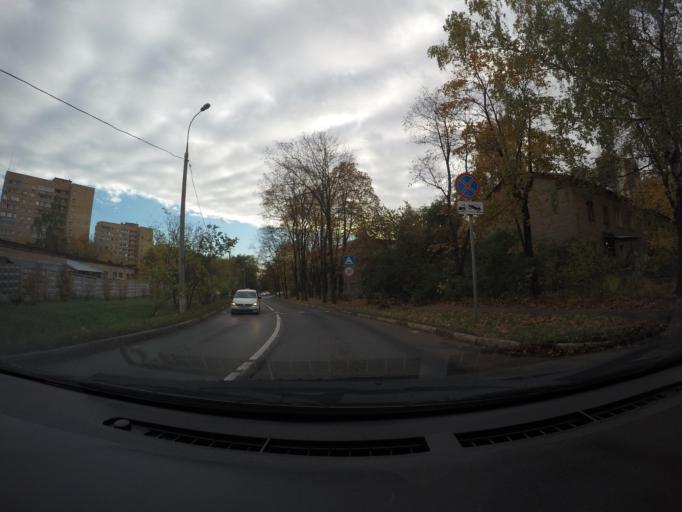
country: RU
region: Moskovskaya
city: Mytishchi
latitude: 55.9179
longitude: 37.7423
